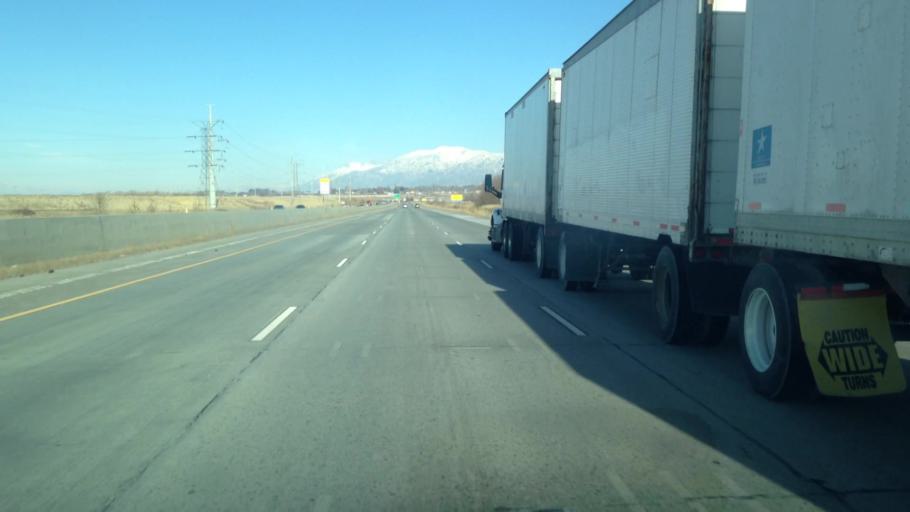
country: US
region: Utah
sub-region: Box Elder County
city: South Willard
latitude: 41.3766
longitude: -112.0424
